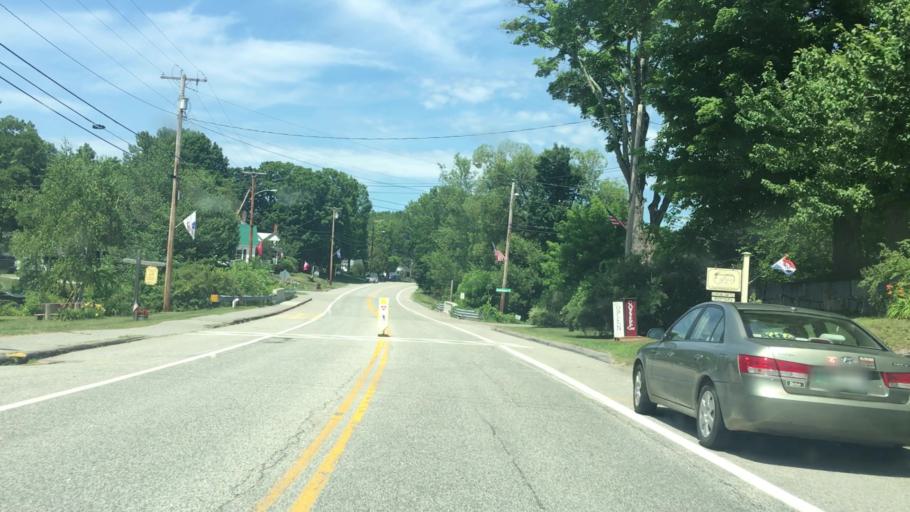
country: US
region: Maine
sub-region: Kennebec County
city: Wayne
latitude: 44.3491
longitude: -70.0677
